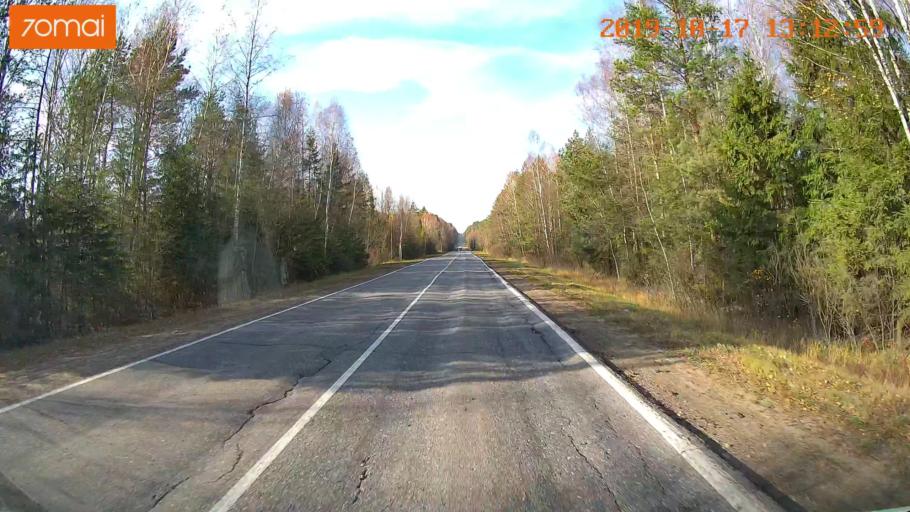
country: RU
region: Rjazan
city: Gus'-Zheleznyy
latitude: 55.0412
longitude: 41.2008
